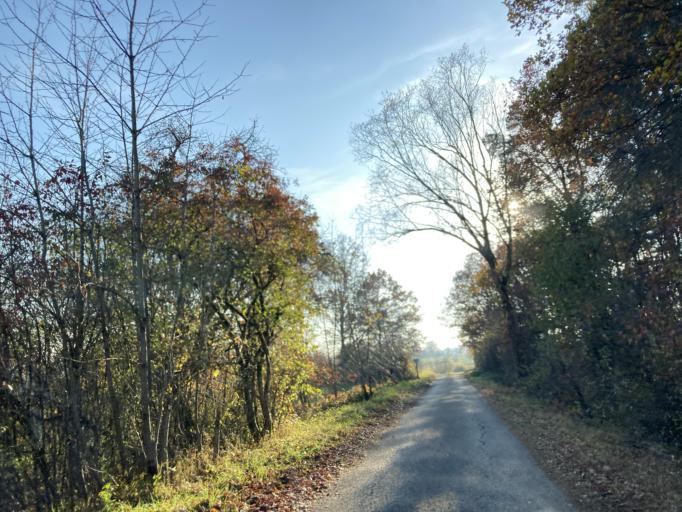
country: DE
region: Baden-Wuerttemberg
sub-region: Tuebingen Region
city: Rottenburg
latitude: 48.5395
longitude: 8.9757
